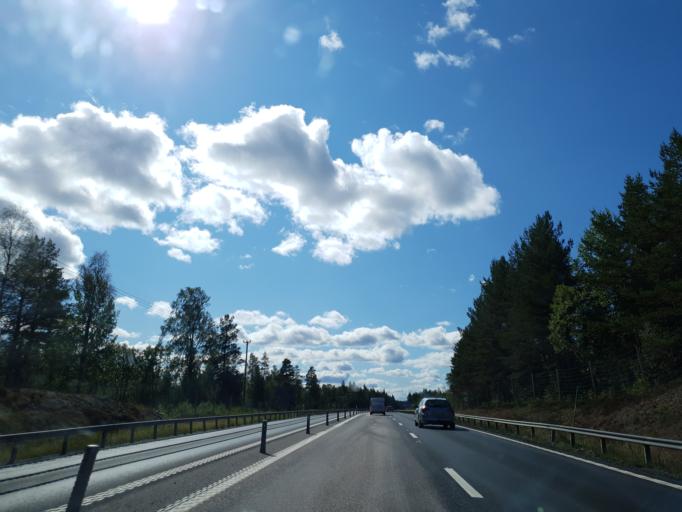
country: SE
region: Vaesterbotten
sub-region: Nordmalings Kommun
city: Nordmaling
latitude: 63.4912
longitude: 19.3149
